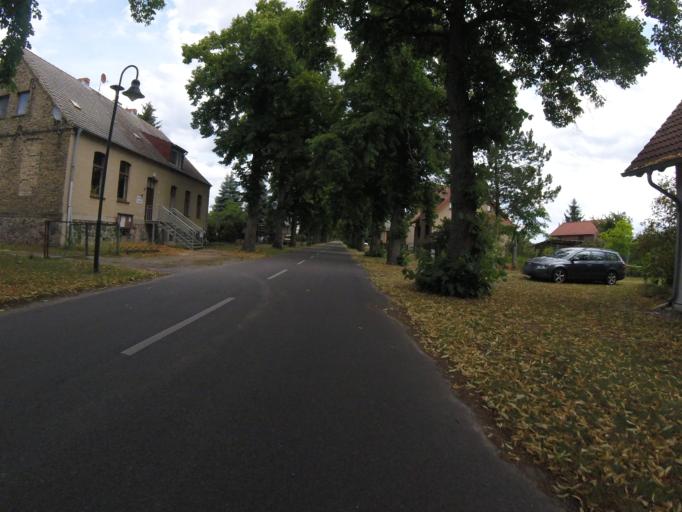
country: DE
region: Brandenburg
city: Gross Koris
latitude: 52.1472
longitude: 13.6860
